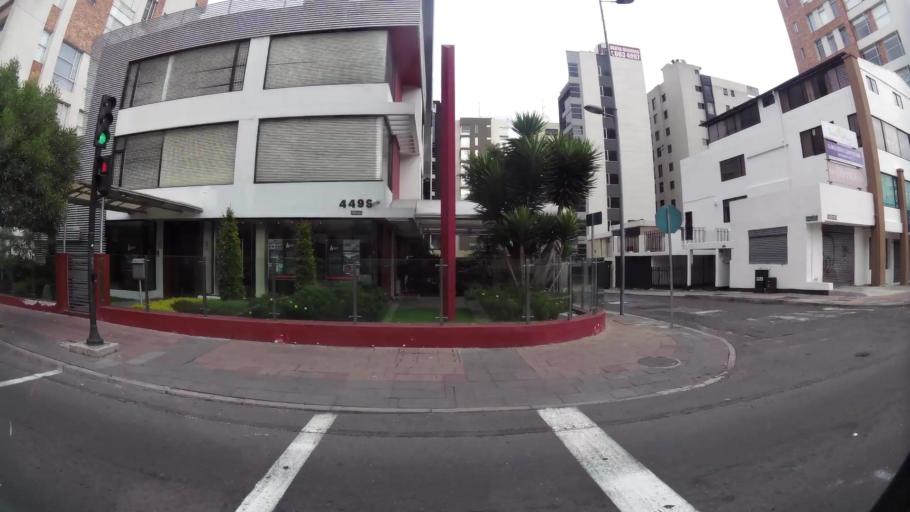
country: EC
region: Pichincha
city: Quito
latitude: -0.1808
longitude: -78.4787
